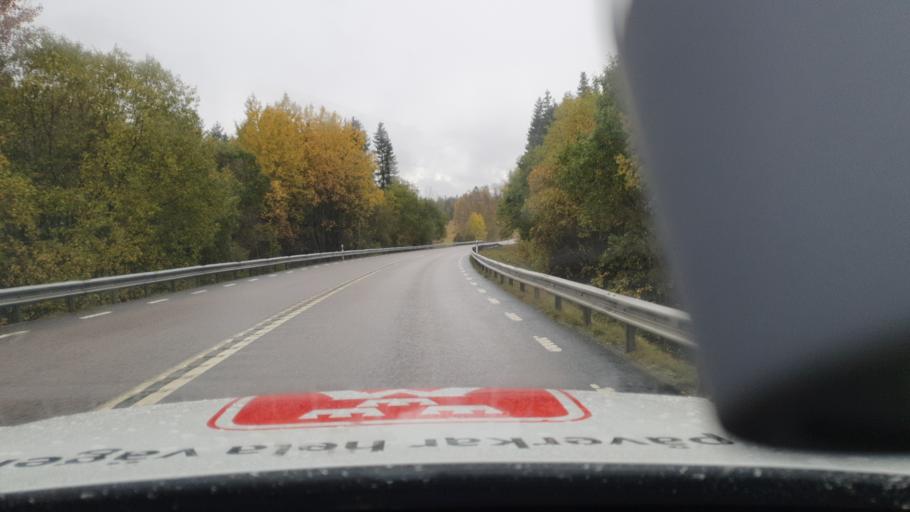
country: SE
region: Vaestra Goetaland
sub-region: Dals-Ed Kommun
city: Ed
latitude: 58.8993
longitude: 11.9740
